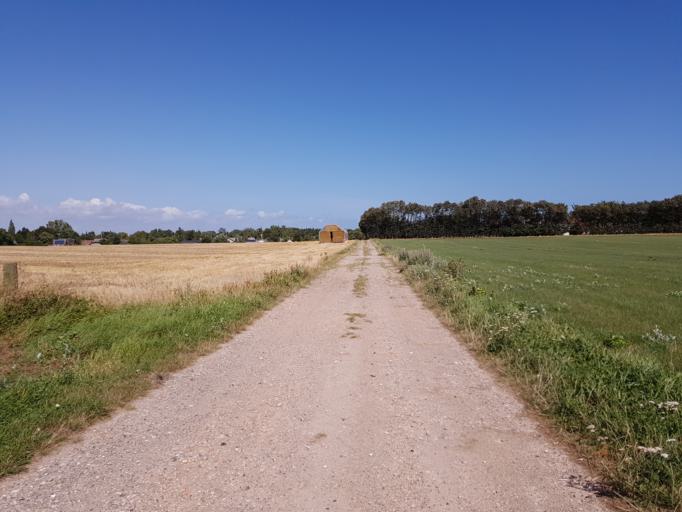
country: DK
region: Zealand
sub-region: Guldborgsund Kommune
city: Nykobing Falster
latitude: 54.5965
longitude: 11.9396
